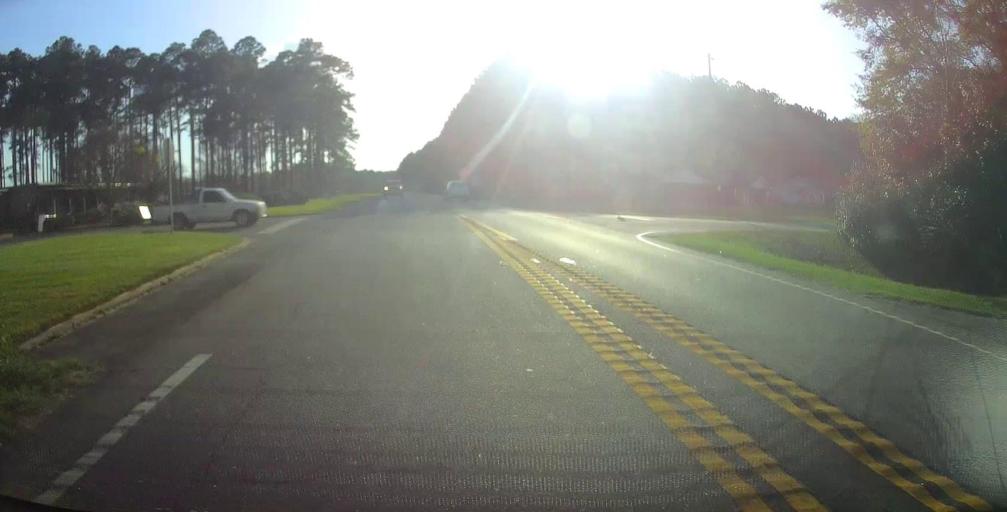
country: US
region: Georgia
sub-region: Tattnall County
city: Reidsville
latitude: 32.0997
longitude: -82.1033
